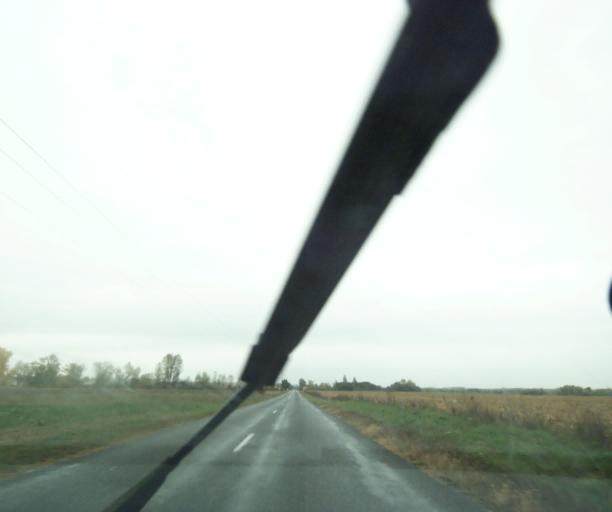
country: FR
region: Rhone-Alpes
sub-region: Departement de l'Ain
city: Loyettes
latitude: 45.7992
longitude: 5.2118
